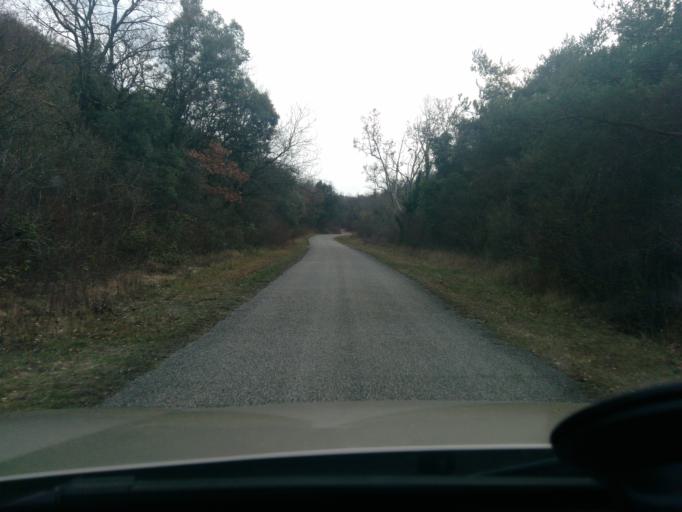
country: FR
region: Rhone-Alpes
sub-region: Departement de l'Ardeche
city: Cruas
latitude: 44.6618
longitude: 4.7425
